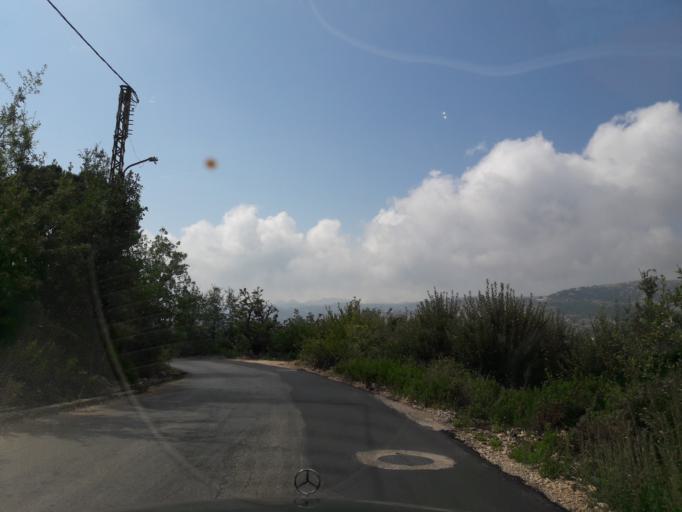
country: LB
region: Mont-Liban
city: Djounie
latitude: 33.9513
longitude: 35.7758
